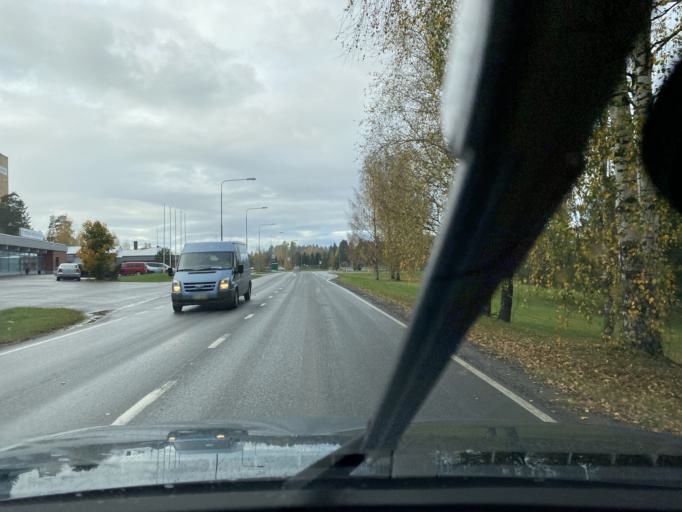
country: FI
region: Haeme
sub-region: Forssa
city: Forssa
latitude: 60.8237
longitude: 23.6016
